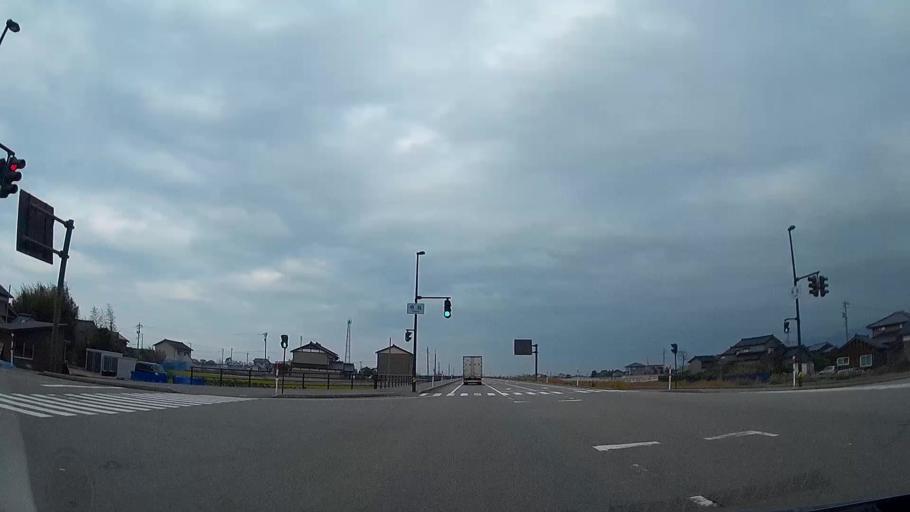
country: JP
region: Toyama
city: Nyuzen
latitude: 36.9209
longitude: 137.4667
